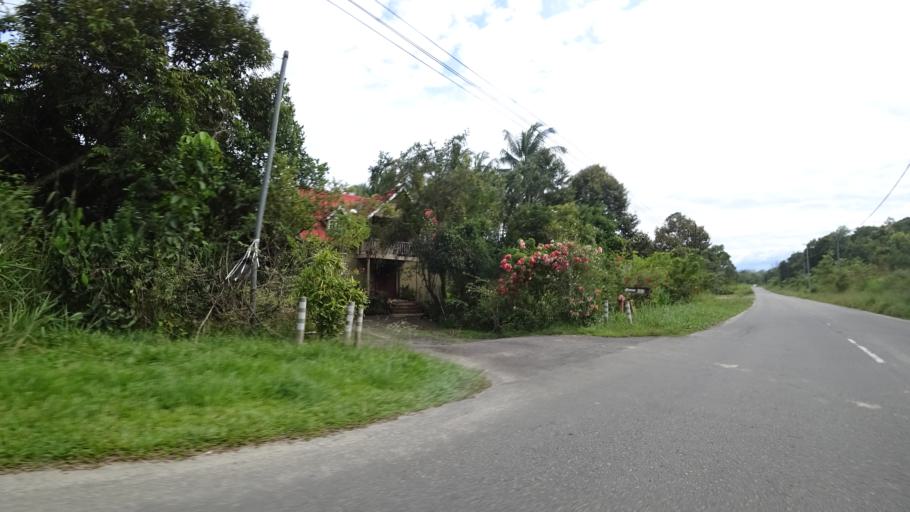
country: BN
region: Brunei and Muara
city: Bandar Seri Begawan
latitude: 4.8433
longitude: 114.9520
